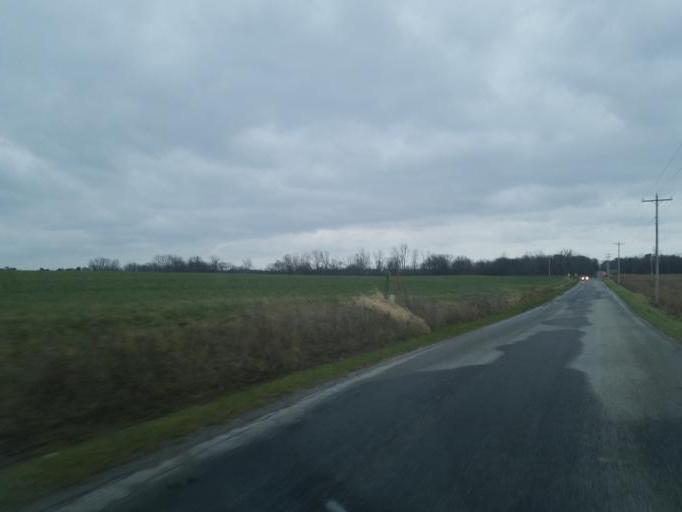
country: US
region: Ohio
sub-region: Morrow County
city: Mount Gilead
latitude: 40.5756
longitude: -82.7576
